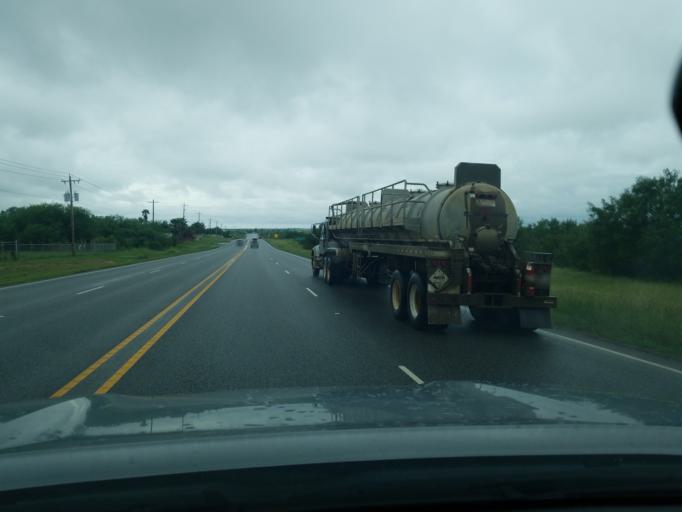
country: US
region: Texas
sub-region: Dimmit County
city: Carrizo Springs
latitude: 28.5282
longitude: -99.8348
